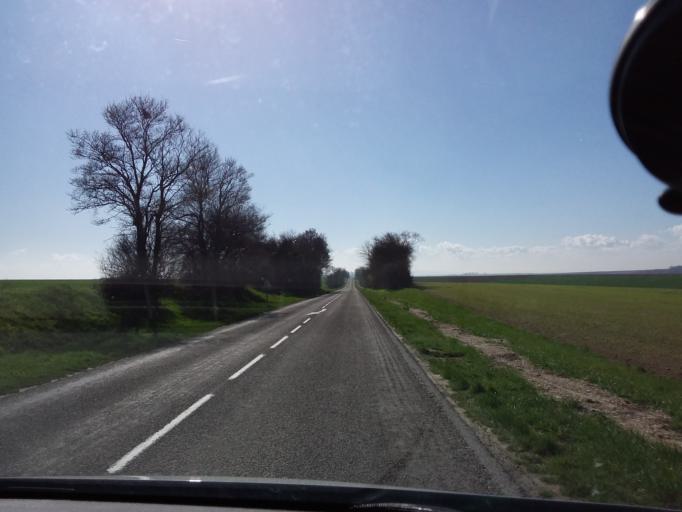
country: FR
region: Picardie
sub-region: Departement de l'Aisne
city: Guignicourt
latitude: 49.4778
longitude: 4.0416
